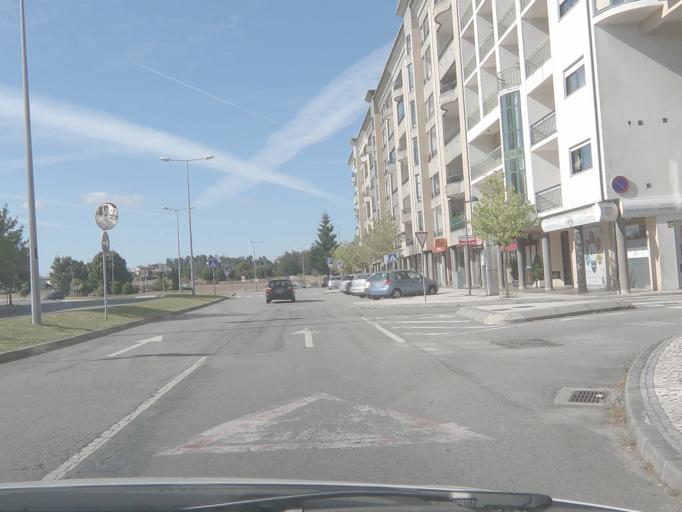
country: PT
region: Viseu
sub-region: Viseu
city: Viseu
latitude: 40.6366
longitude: -7.9291
